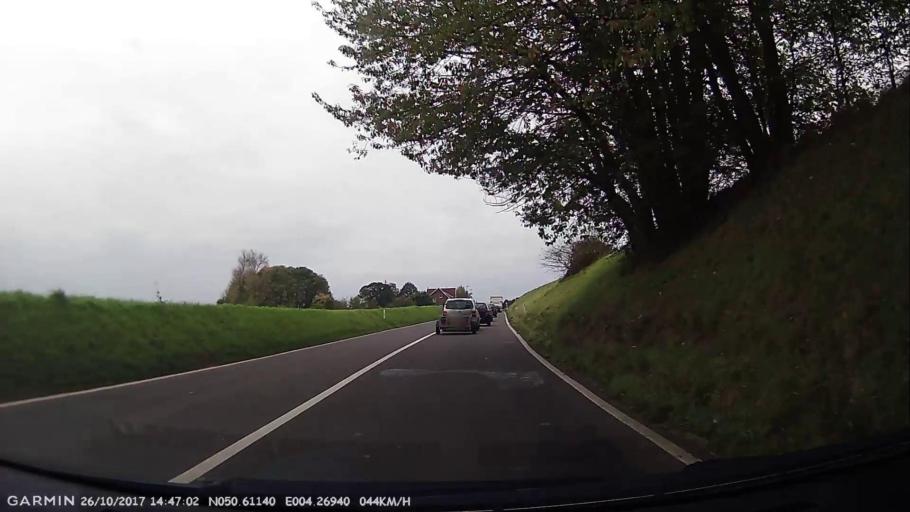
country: BE
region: Wallonia
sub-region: Province du Brabant Wallon
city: Ittre
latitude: 50.6114
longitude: 4.2693
